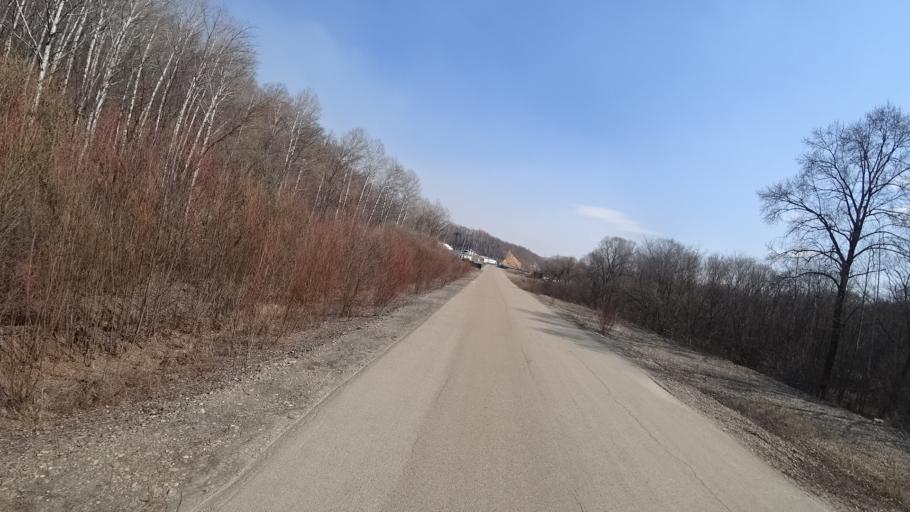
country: RU
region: Amur
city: Novobureyskiy
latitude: 49.7963
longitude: 129.9581
